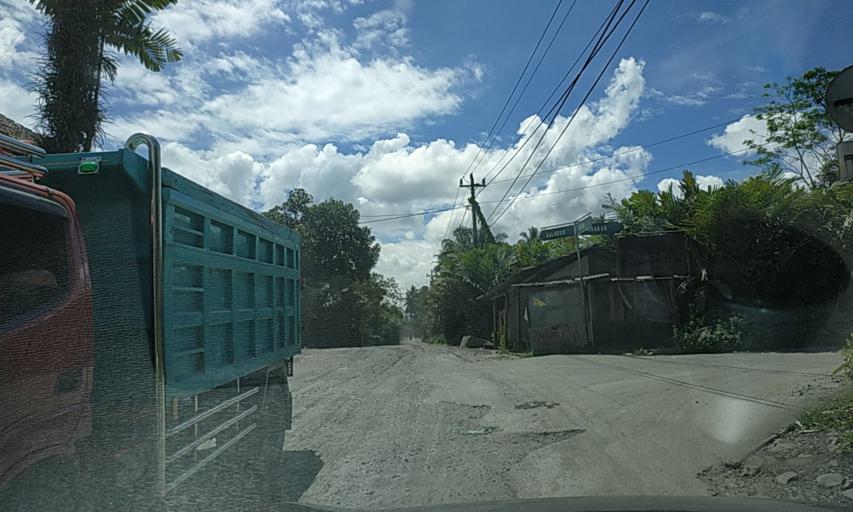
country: ID
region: Central Java
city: Muntilan
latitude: -7.6030
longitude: 110.3584
